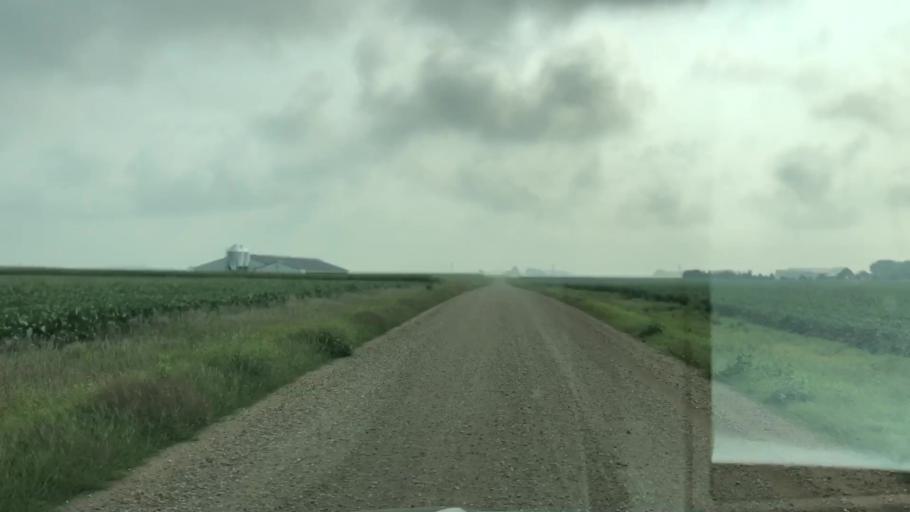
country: US
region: Iowa
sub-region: Sioux County
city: Hull
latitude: 43.2295
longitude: -96.0887
